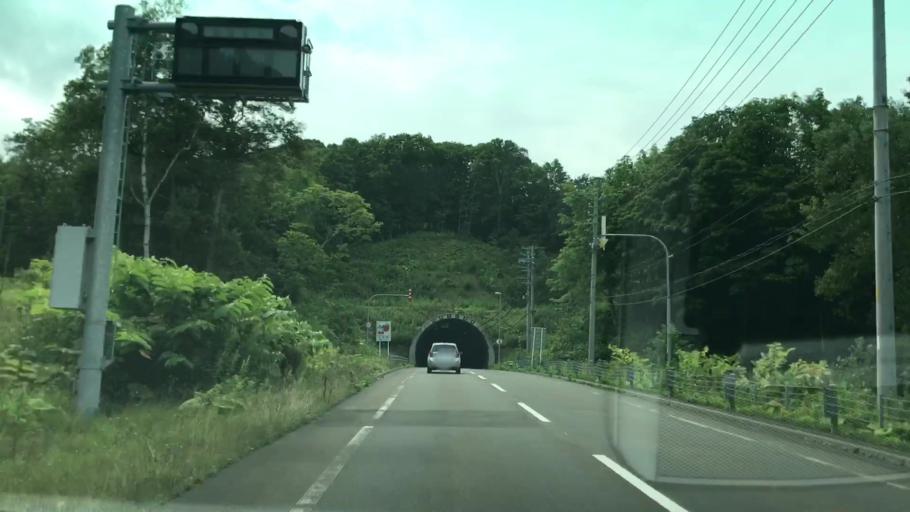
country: JP
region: Hokkaido
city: Yoichi
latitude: 43.1247
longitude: 140.8286
